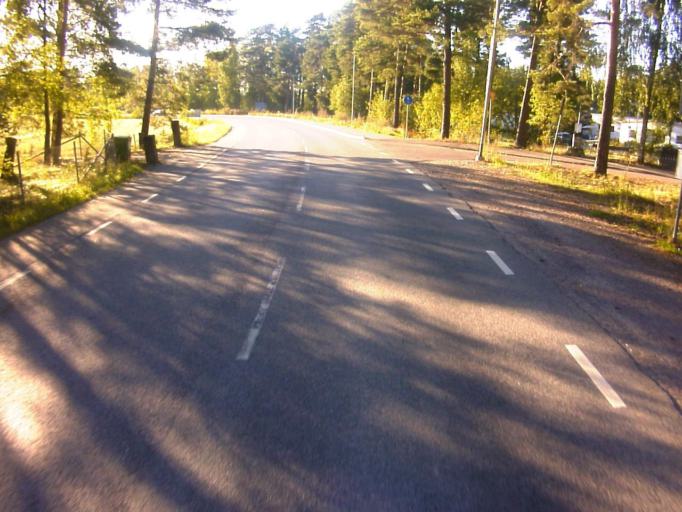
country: SE
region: Soedermanland
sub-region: Eskilstuna Kommun
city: Hallbybrunn
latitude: 59.3991
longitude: 16.4132
